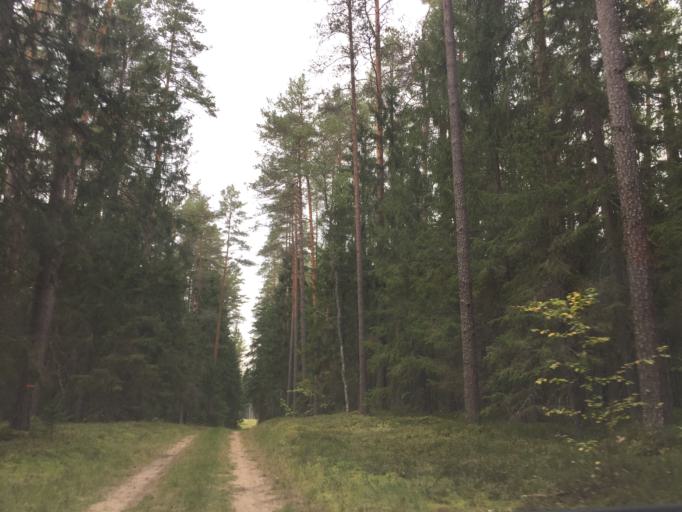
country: LV
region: Baldone
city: Baldone
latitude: 56.7733
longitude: 24.4494
